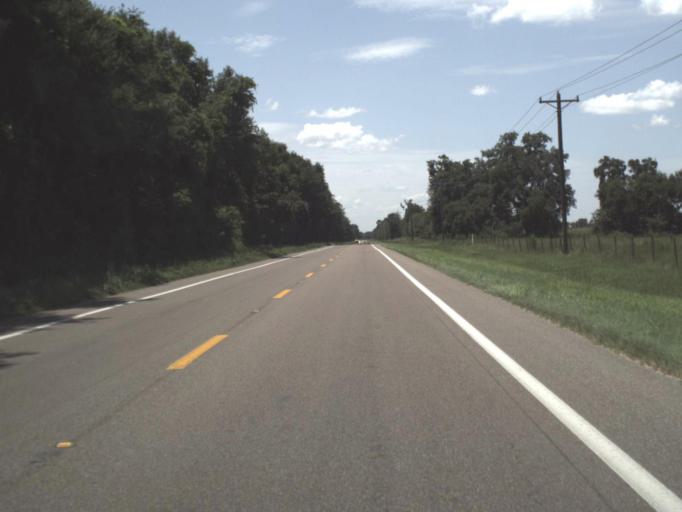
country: US
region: Florida
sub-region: Gilchrist County
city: Trenton
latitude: 29.6481
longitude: -82.8371
